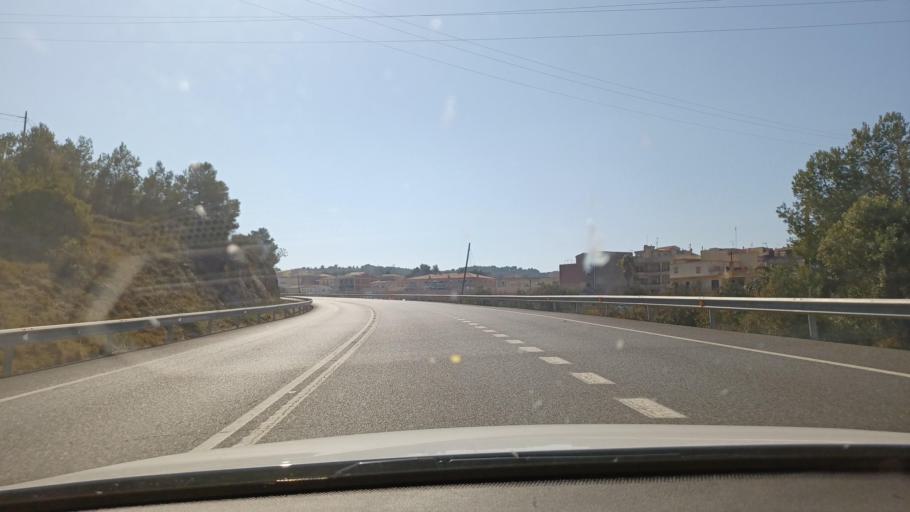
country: ES
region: Catalonia
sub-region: Provincia de Tarragona
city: El Perello
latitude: 40.8746
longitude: 0.7147
